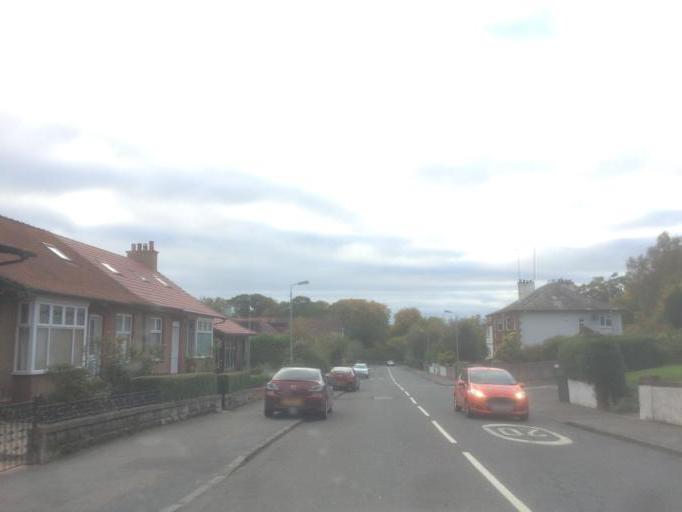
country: GB
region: Scotland
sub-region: East Renfrewshire
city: Giffnock
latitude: 55.8018
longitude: -4.3176
